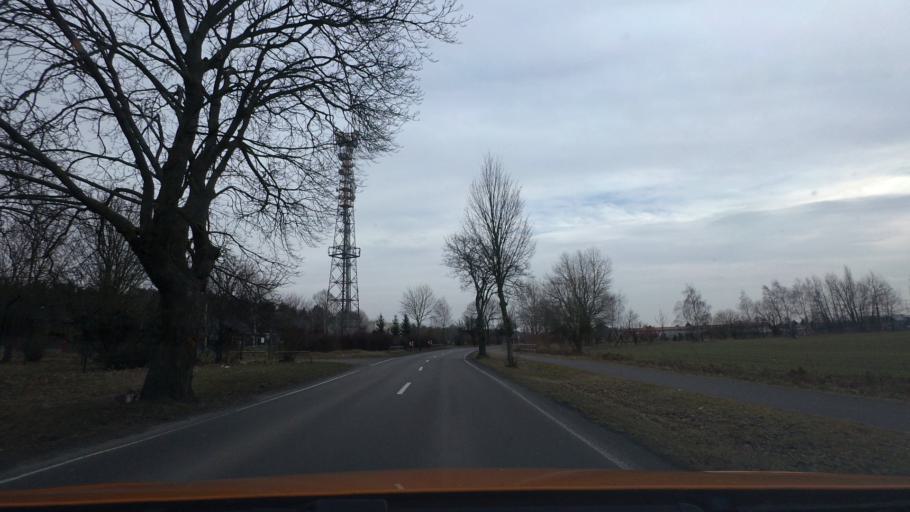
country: DE
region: Brandenburg
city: Ahrensfelde
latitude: 52.5878
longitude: 13.5597
